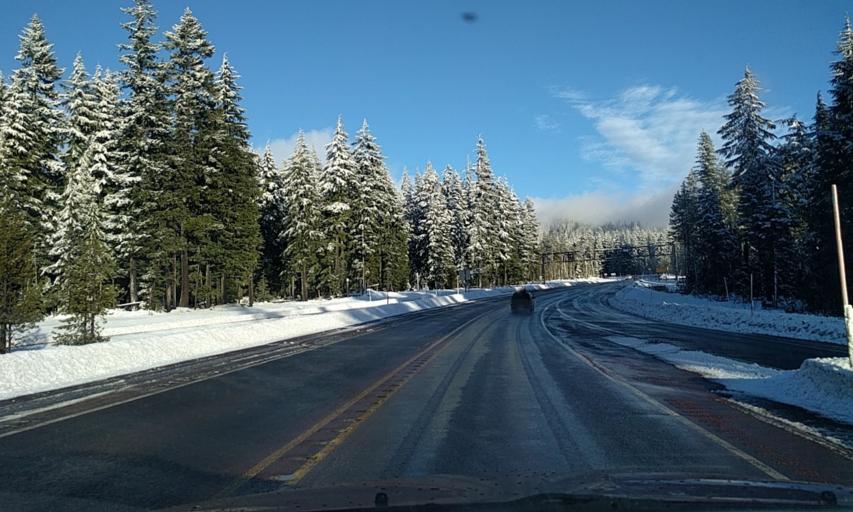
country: US
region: Oregon
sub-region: Clackamas County
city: Mount Hood Village
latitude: 45.2836
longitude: -121.7122
